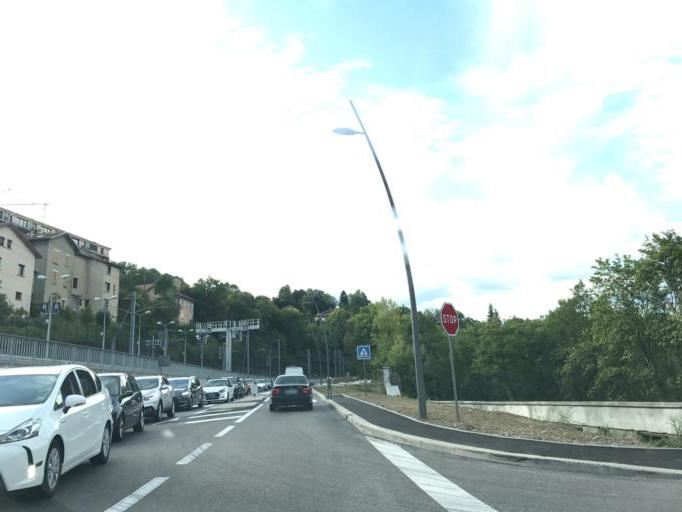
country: FR
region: Rhone-Alpes
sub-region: Departement de l'Ain
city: Bellegarde-sur-Valserine
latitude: 46.1141
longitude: 5.8246
